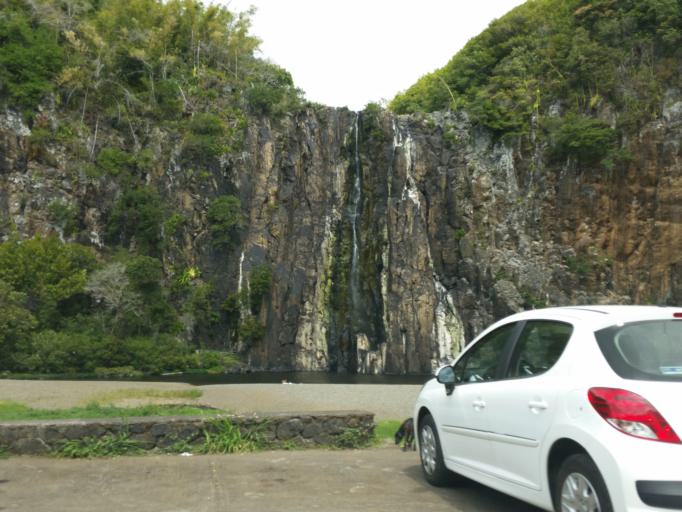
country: RE
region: Reunion
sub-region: Reunion
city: Sainte-Suzanne
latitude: -20.9197
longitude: 55.6043
